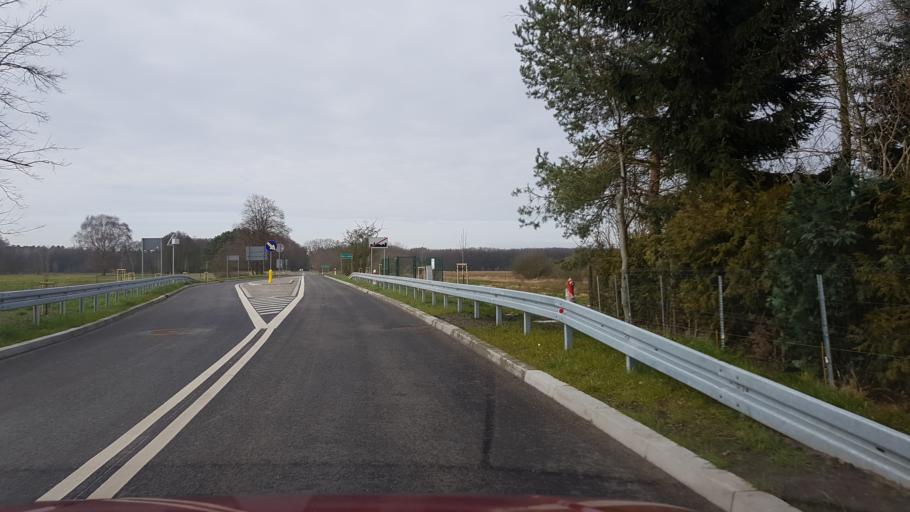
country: PL
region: West Pomeranian Voivodeship
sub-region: Powiat policki
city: Nowe Warpno
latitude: 53.6962
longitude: 14.3514
